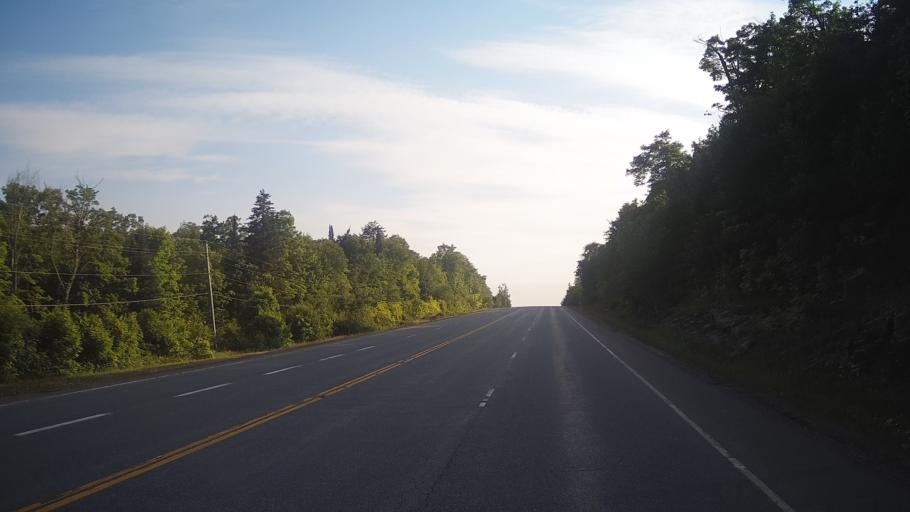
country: CA
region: Ontario
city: Huntsville
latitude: 45.4107
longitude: -78.8644
